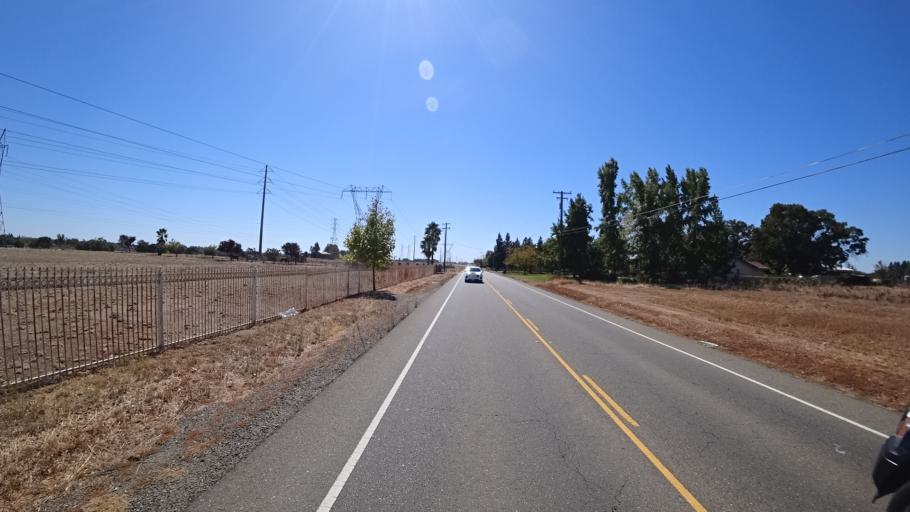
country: US
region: California
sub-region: Sacramento County
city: Vineyard
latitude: 38.4436
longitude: -121.3532
